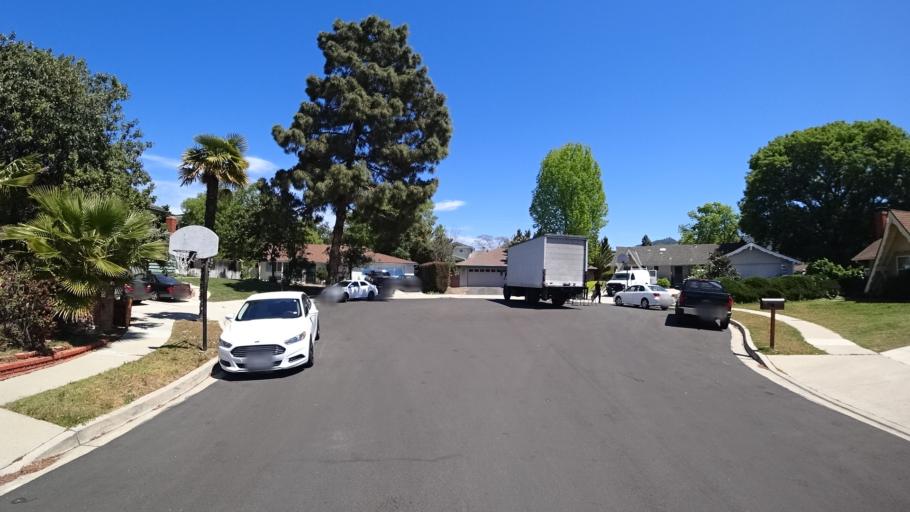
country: US
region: California
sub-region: Ventura County
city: Casa Conejo
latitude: 34.1634
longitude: -118.9541
